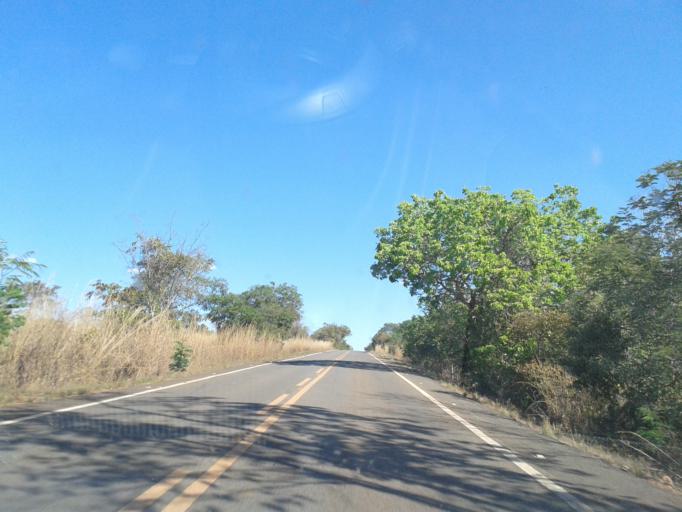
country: BR
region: Goias
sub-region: Crixas
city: Crixas
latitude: -14.0026
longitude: -50.3249
